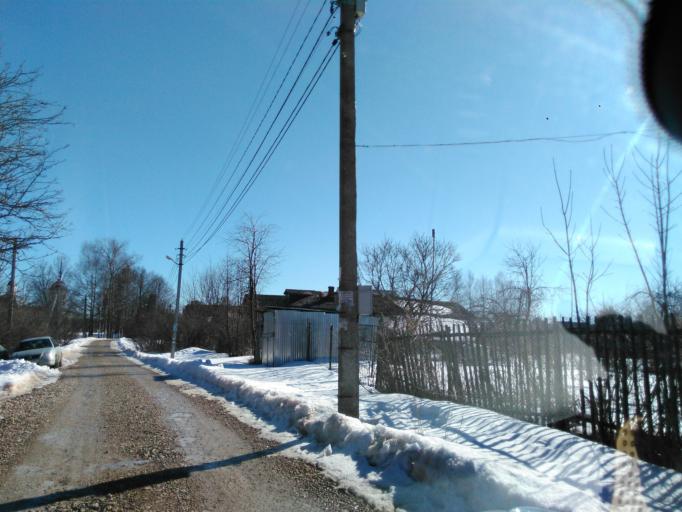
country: RU
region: Moskovskaya
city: Yermolino
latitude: 56.1530
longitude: 37.4580
